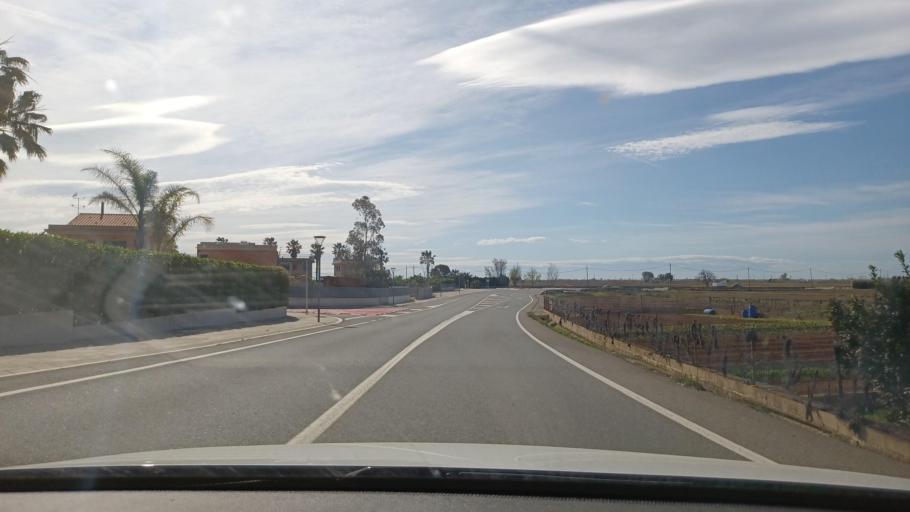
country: ES
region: Catalonia
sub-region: Provincia de Tarragona
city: L'Ampolla
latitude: 40.7998
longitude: 0.6952
